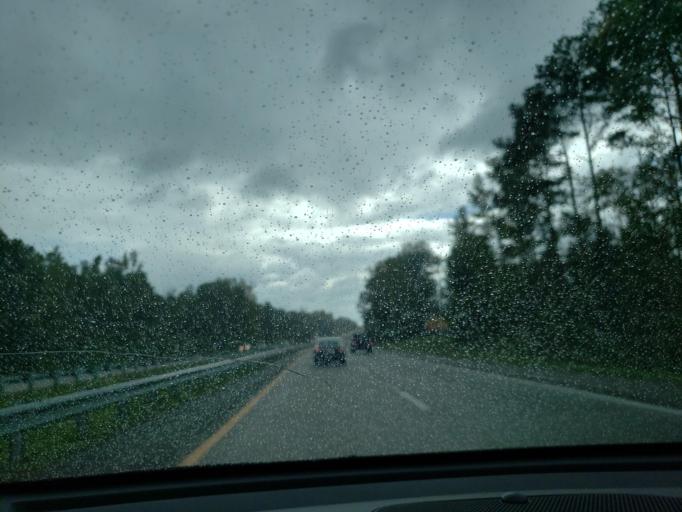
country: US
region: North Carolina
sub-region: Warren County
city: Norlina
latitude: 36.5007
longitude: -78.2164
